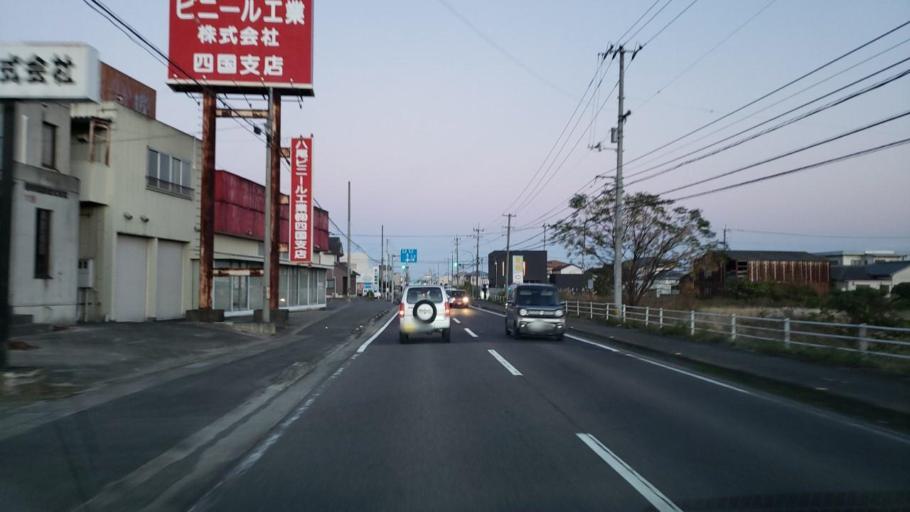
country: JP
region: Tokushima
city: Ishii
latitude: 34.1216
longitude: 134.4486
